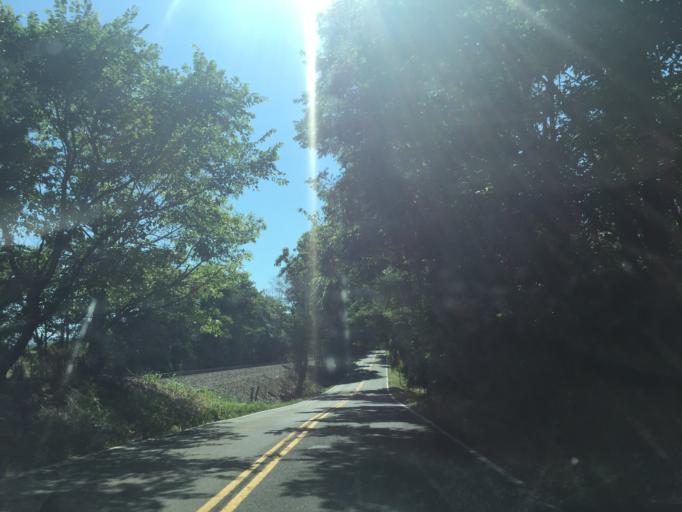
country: US
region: Virginia
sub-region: Warren County
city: Front Royal
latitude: 38.9293
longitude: -78.1603
